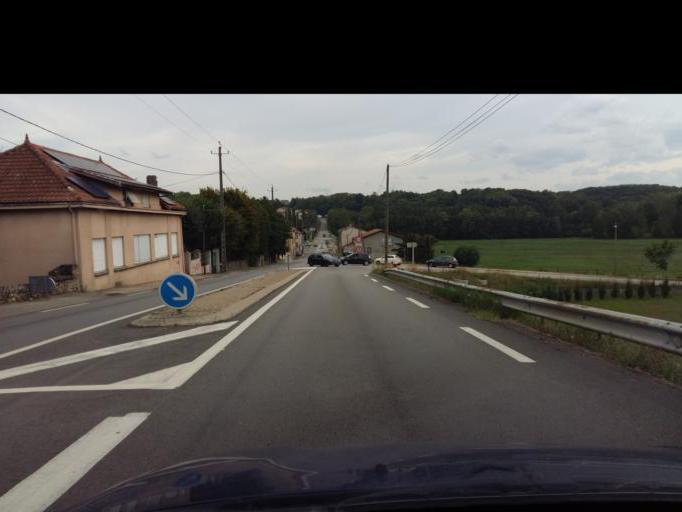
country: FR
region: Rhone-Alpes
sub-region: Departement de l'Isere
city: Auberives-sur-Vareze
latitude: 45.4333
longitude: 4.8182
